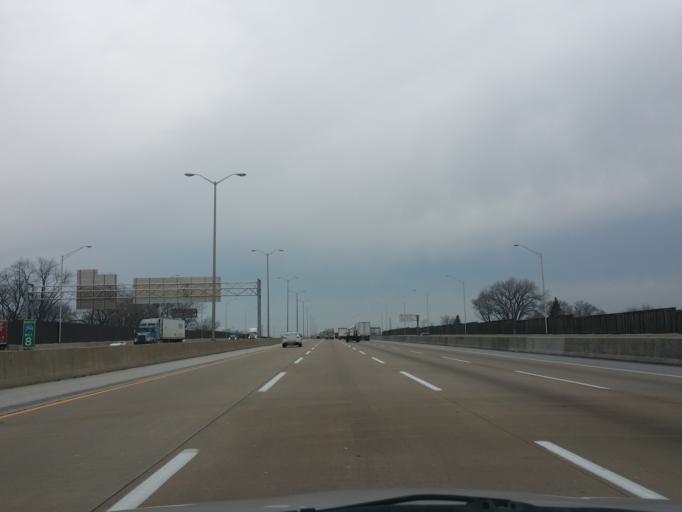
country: US
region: Illinois
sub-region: Cook County
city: Posen
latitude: 41.6231
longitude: -87.6896
